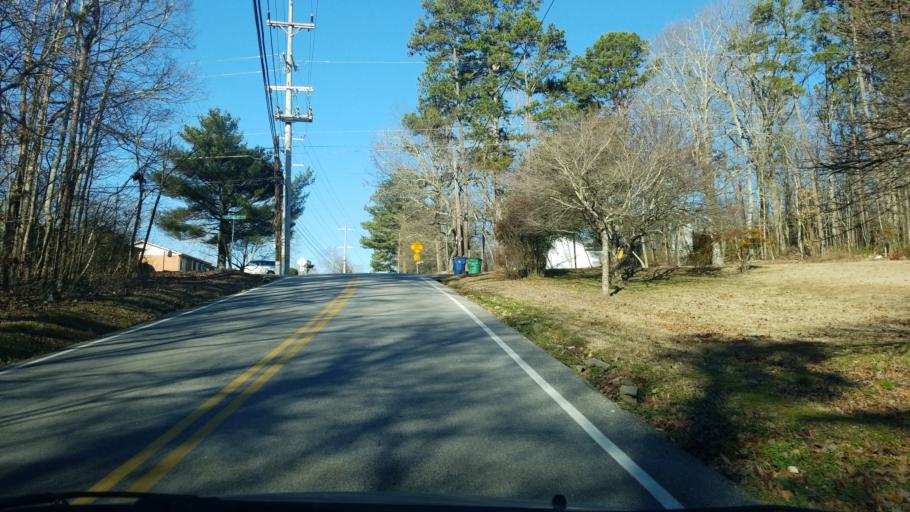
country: US
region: Tennessee
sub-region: Hamilton County
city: Collegedale
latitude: 35.0389
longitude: -85.0922
